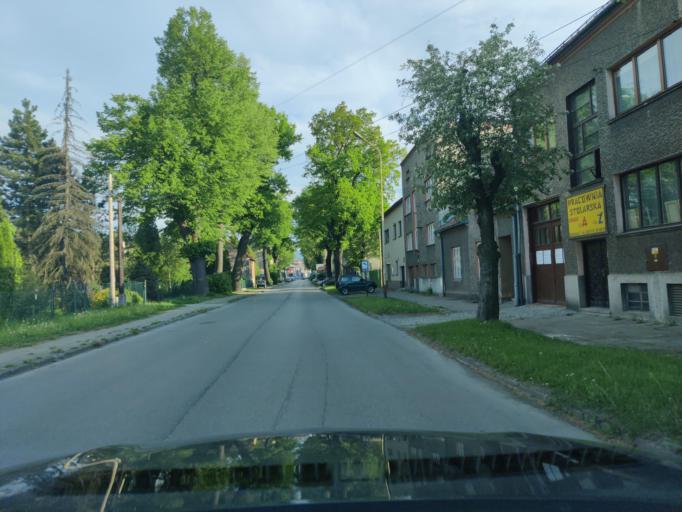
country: PL
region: Silesian Voivodeship
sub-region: Powiat zywiecki
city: Zywiec
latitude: 49.6949
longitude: 19.2026
